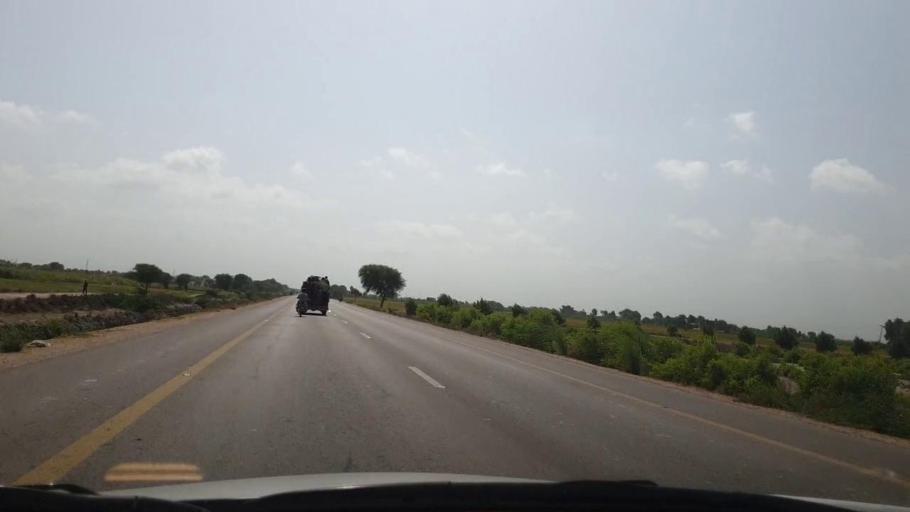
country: PK
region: Sindh
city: Matli
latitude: 24.9812
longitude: 68.6660
